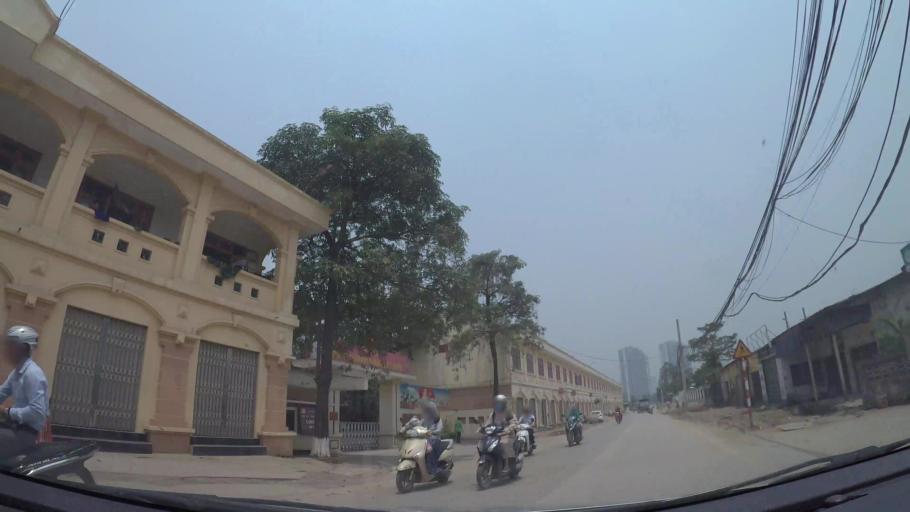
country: VN
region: Ha Noi
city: Ha Dong
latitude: 20.9987
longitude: 105.7640
